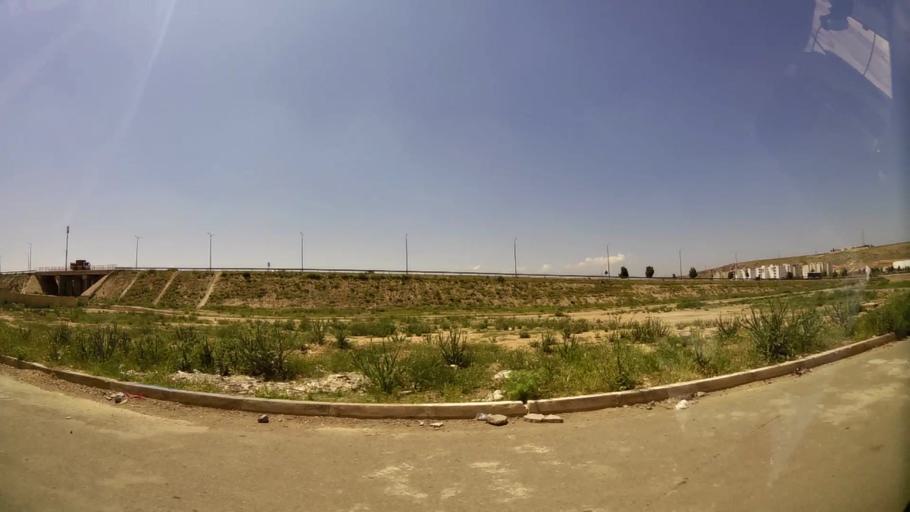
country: MA
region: Oriental
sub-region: Oujda-Angad
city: Oujda
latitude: 34.6948
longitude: -1.9408
